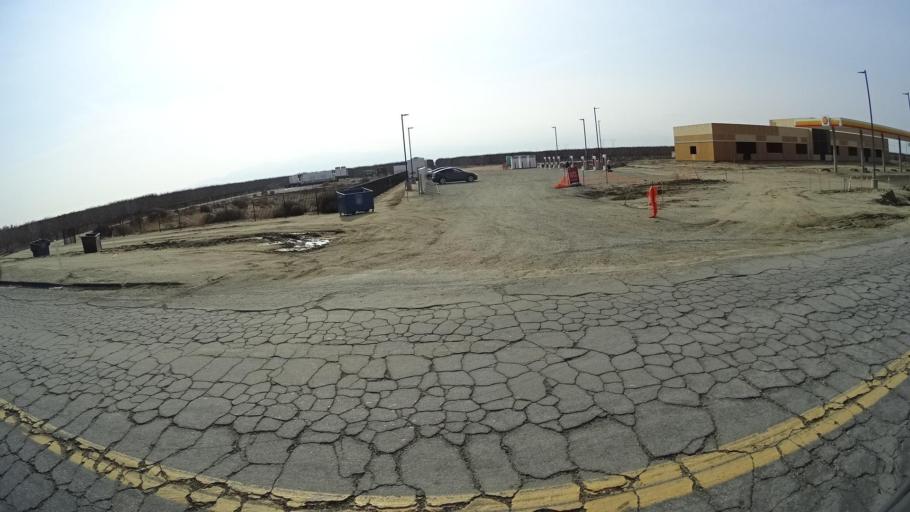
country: US
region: California
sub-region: Kern County
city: Greenfield
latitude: 35.0951
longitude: -119.0398
